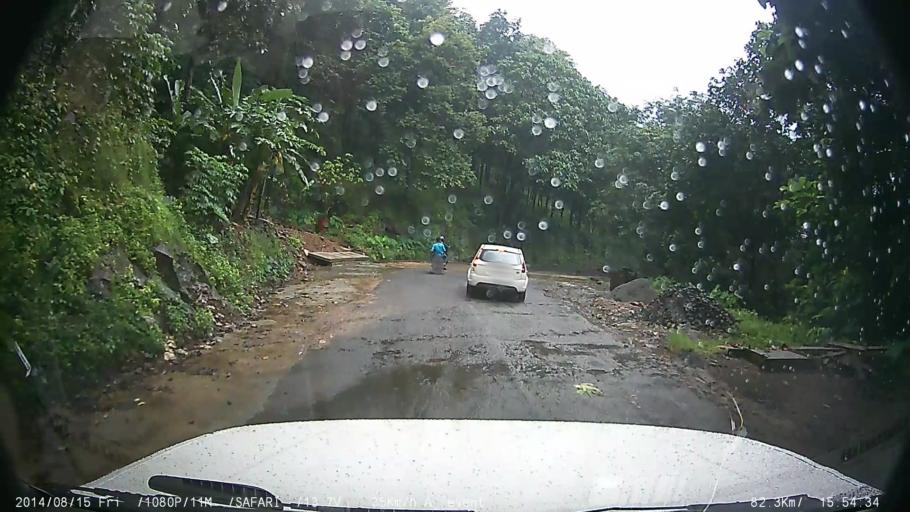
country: IN
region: Kerala
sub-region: Kottayam
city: Lalam
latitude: 9.7958
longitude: 76.7282
